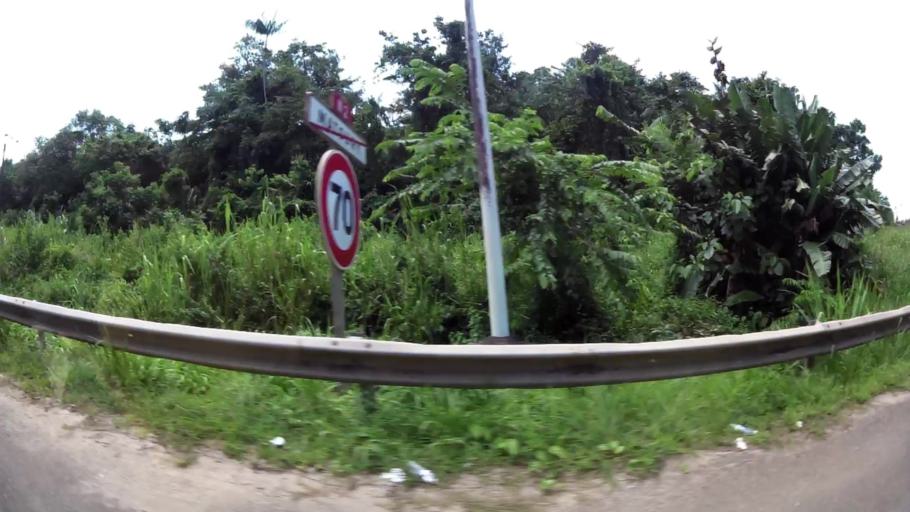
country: GF
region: Guyane
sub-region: Guyane
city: Matoury
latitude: 4.8567
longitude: -52.3342
